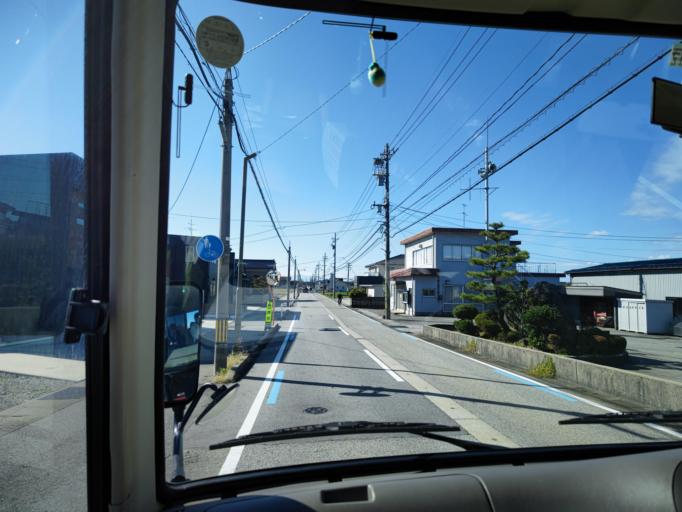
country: JP
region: Toyama
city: Nyuzen
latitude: 36.9027
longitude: 137.4234
